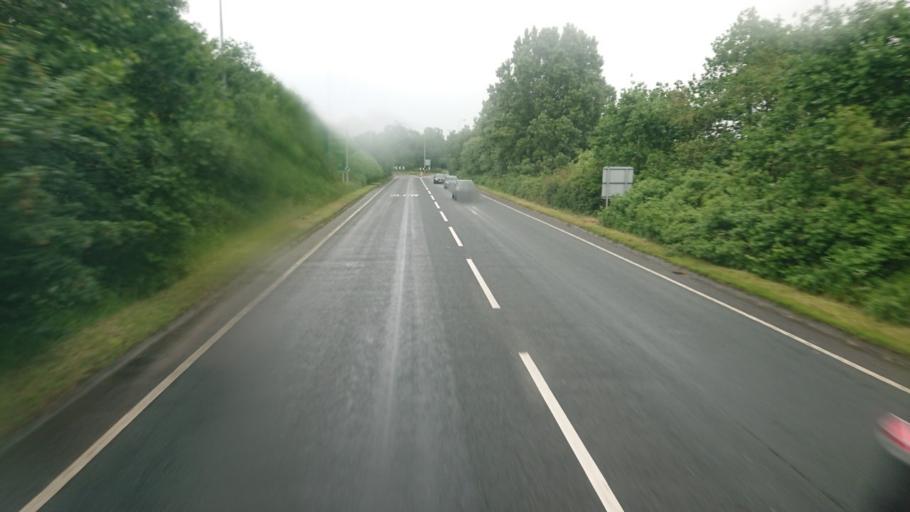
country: GB
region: England
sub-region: Lancashire
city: Morecambe
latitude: 54.0421
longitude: -2.8578
